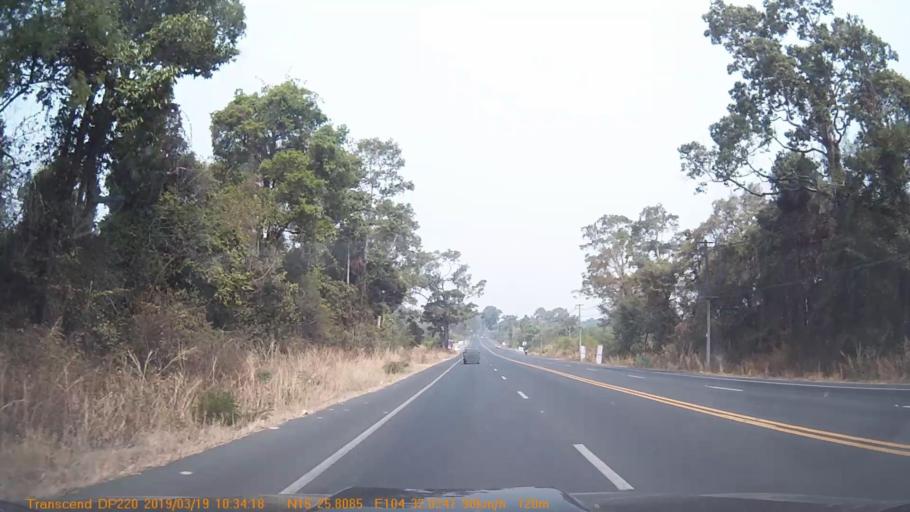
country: TH
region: Changwat Ubon Ratchathani
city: Khueang Nai
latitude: 15.4304
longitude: 104.5336
